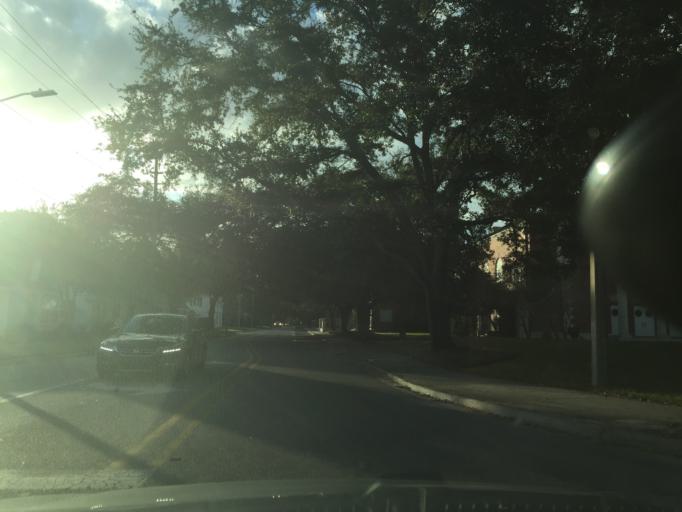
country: US
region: Florida
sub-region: Hillsborough County
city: Tampa
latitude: 27.9339
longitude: -82.4934
